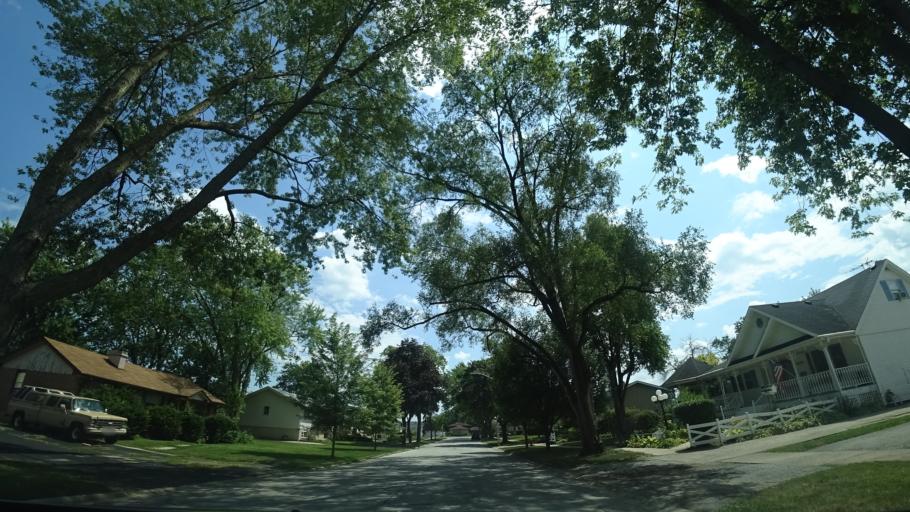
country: US
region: Illinois
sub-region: Cook County
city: Alsip
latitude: 41.6759
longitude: -87.7234
